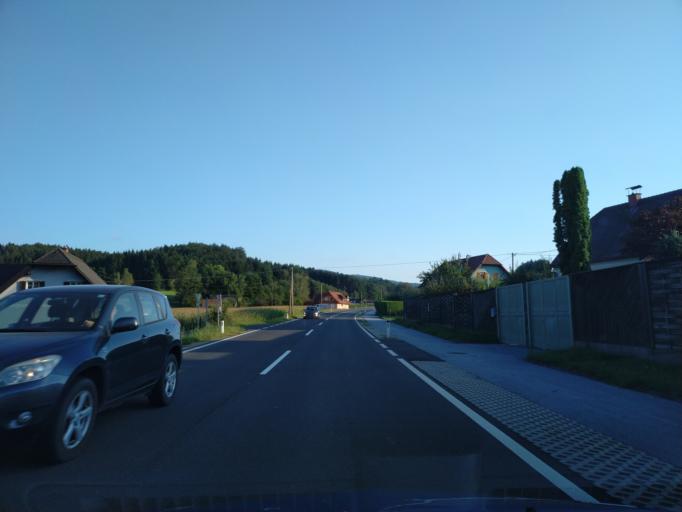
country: AT
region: Styria
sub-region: Politischer Bezirk Deutschlandsberg
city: Pitschgau
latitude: 46.7142
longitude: 15.2528
